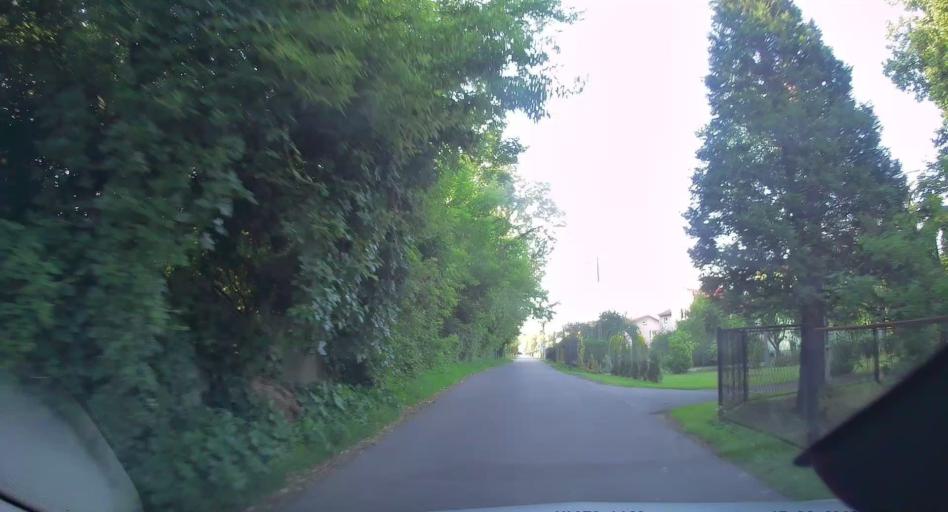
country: PL
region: Lesser Poland Voivodeship
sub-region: Powiat oswiecimski
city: Babice
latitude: 50.0729
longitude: 19.1863
